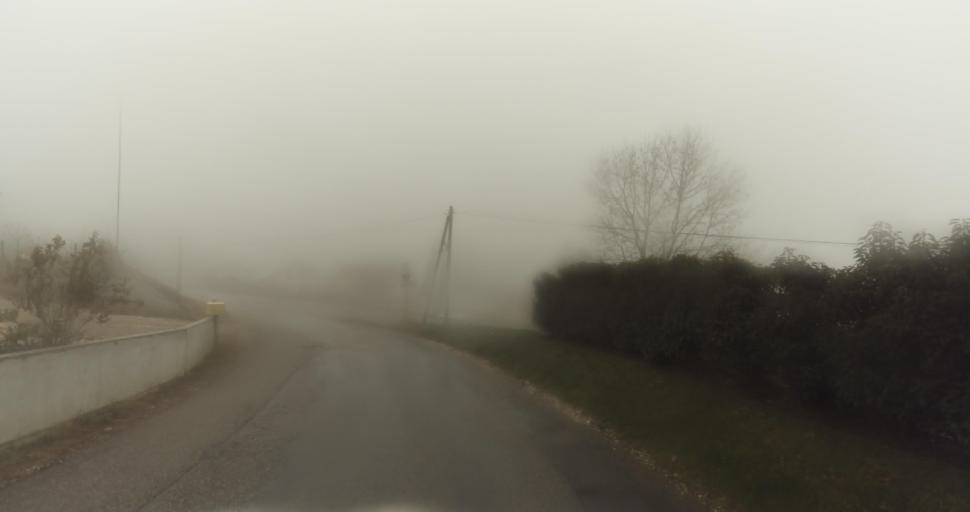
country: FR
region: Rhone-Alpes
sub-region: Departement de la Haute-Savoie
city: Thorens-Glieres
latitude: 45.9753
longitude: 6.2166
